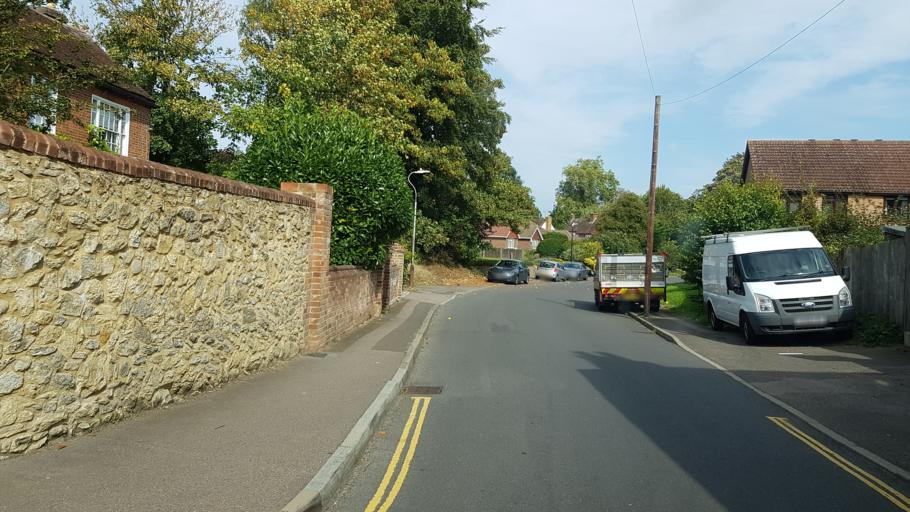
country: GB
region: England
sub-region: Kent
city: Larkfield
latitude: 51.2896
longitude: 0.4302
